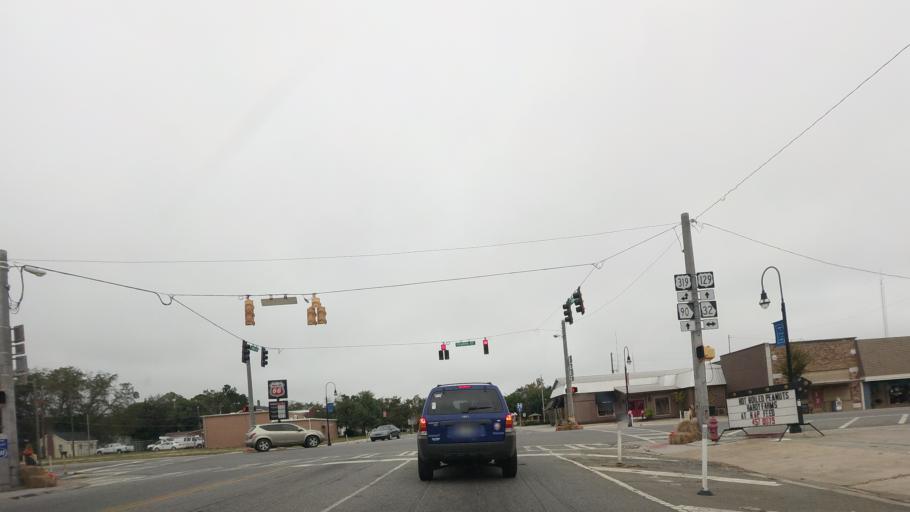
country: US
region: Georgia
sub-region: Irwin County
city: Ocilla
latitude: 31.5940
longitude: -83.2505
